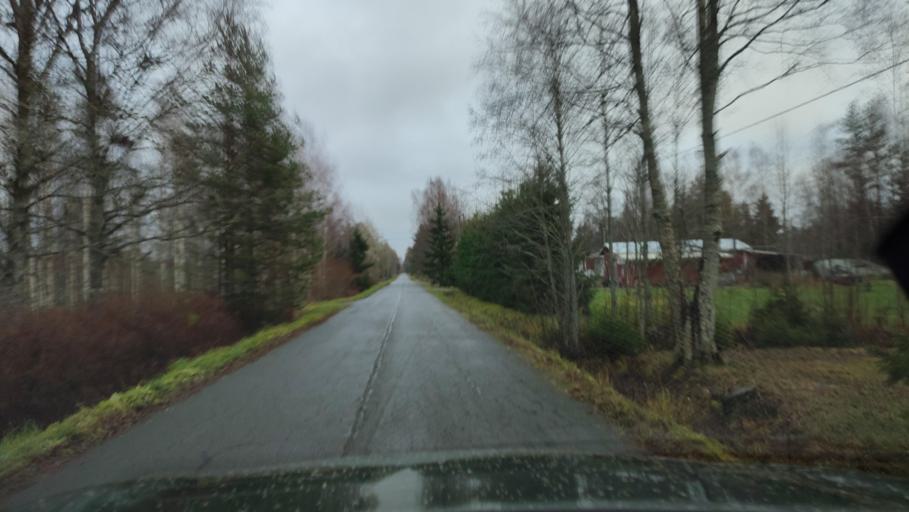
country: FI
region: Southern Ostrobothnia
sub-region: Suupohja
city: Teuva
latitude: 62.4573
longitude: 21.5916
